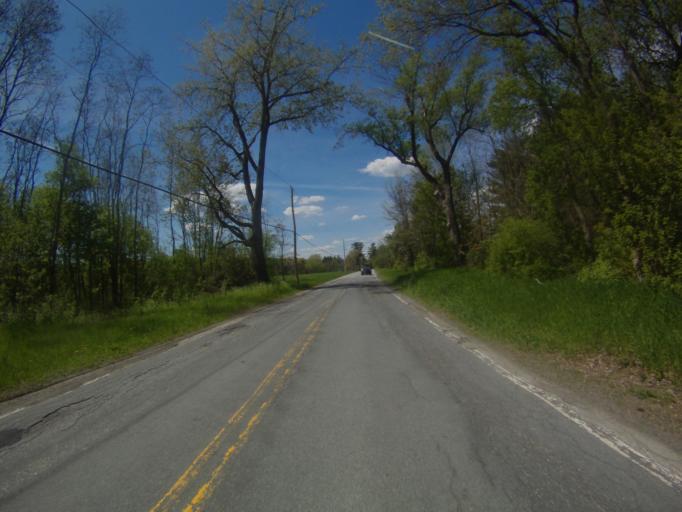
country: US
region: New York
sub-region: Essex County
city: Port Henry
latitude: 43.9629
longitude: -73.4222
